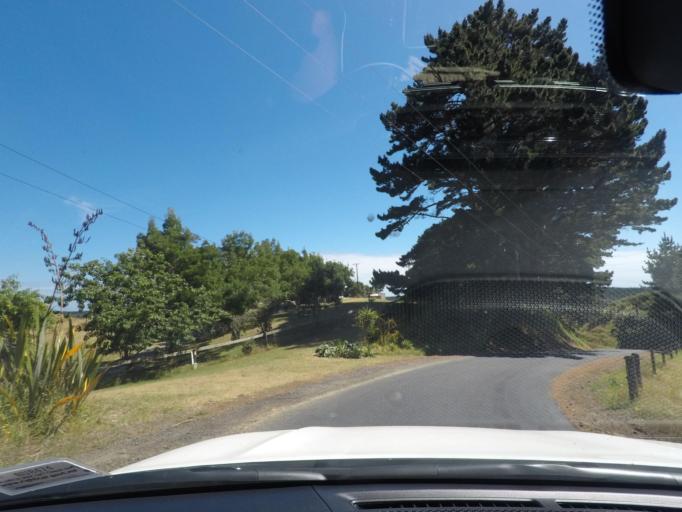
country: NZ
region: Auckland
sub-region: Auckland
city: Parakai
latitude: -36.5893
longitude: 174.2886
